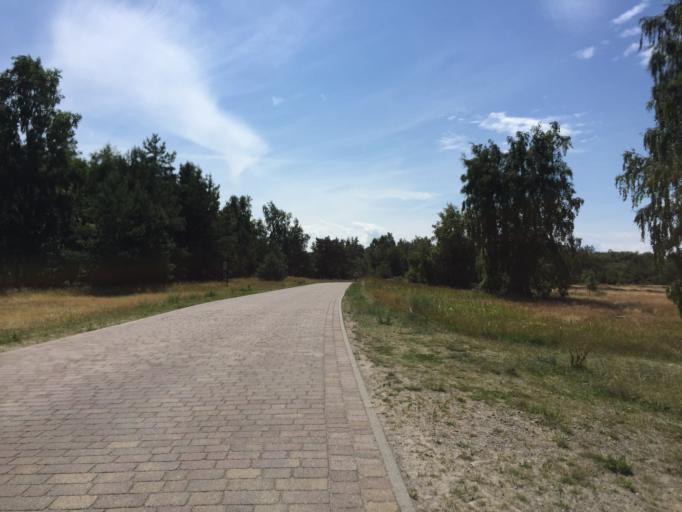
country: DE
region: Mecklenburg-Vorpommern
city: Hiddensee
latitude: 54.5436
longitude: 13.1044
